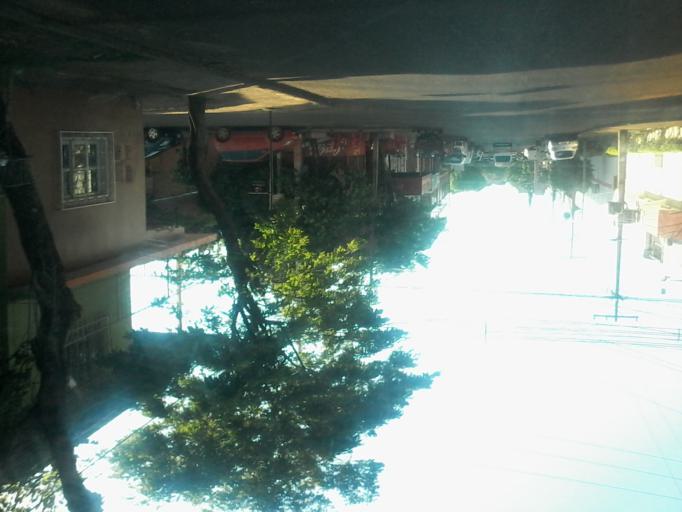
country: PY
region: Alto Parana
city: Ciudad del Este
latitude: -25.5023
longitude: -54.6341
